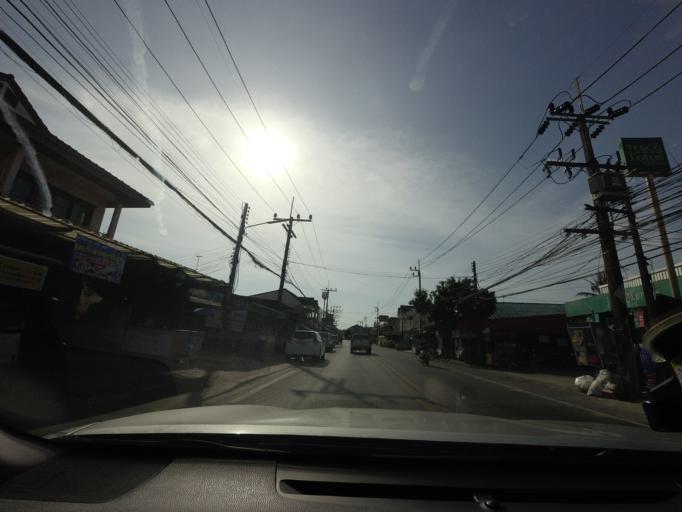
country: TH
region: Phuket
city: Thalang
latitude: 8.0164
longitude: 98.3194
